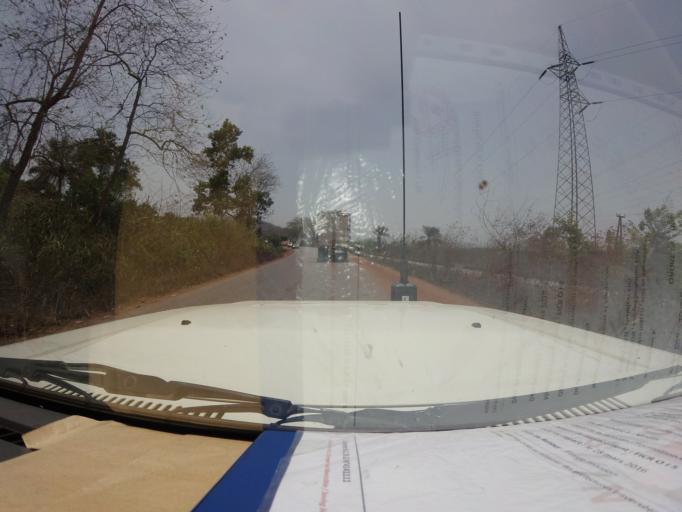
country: GN
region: Kindia
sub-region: Coyah
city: Coyah
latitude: 9.7932
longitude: -13.3032
